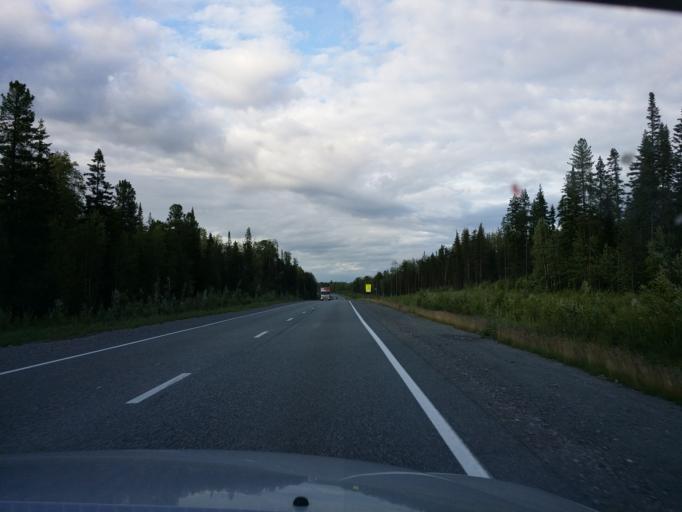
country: RU
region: Khanty-Mansiyskiy Avtonomnyy Okrug
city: Pyt-Yakh
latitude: 60.7018
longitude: 72.5250
